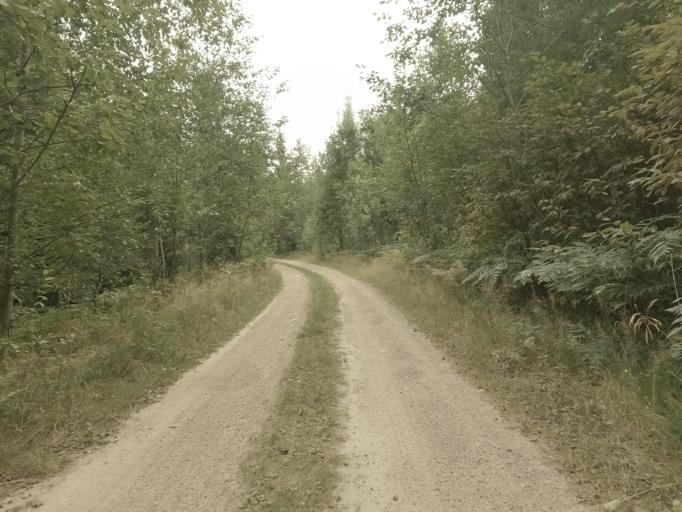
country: RU
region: Leningrad
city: Kamennogorsk
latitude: 61.0050
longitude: 29.1827
